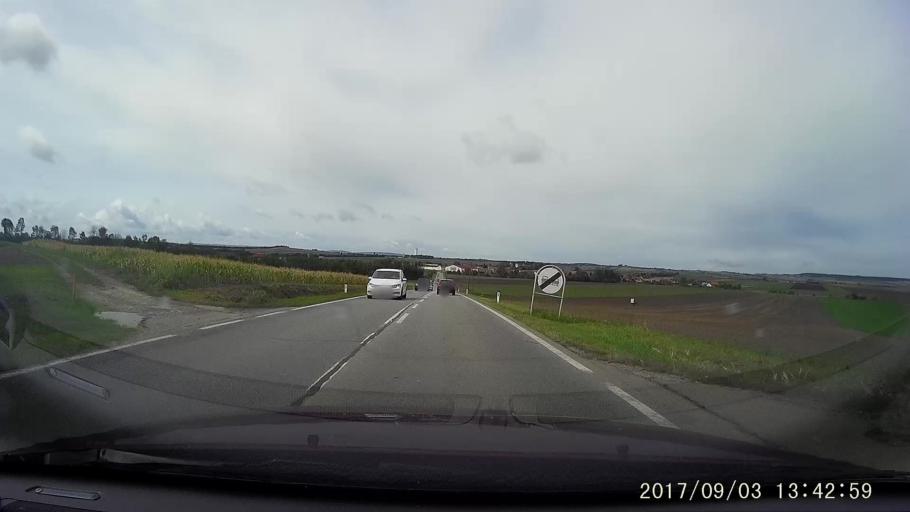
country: AT
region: Lower Austria
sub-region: Politischer Bezirk Hollabrunn
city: Guntersdorf
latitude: 48.6212
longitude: 16.0663
